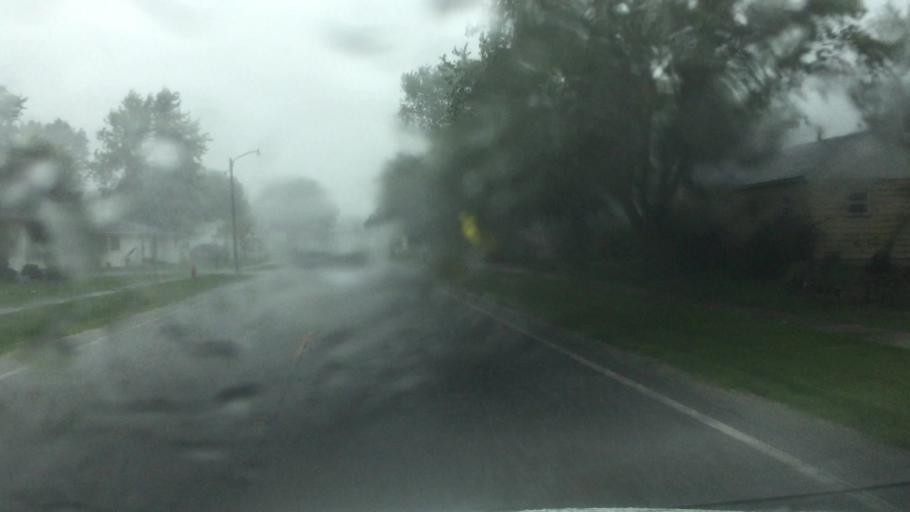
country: US
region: Illinois
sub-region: Adams County
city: Camp Point
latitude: 40.2331
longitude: -91.0646
